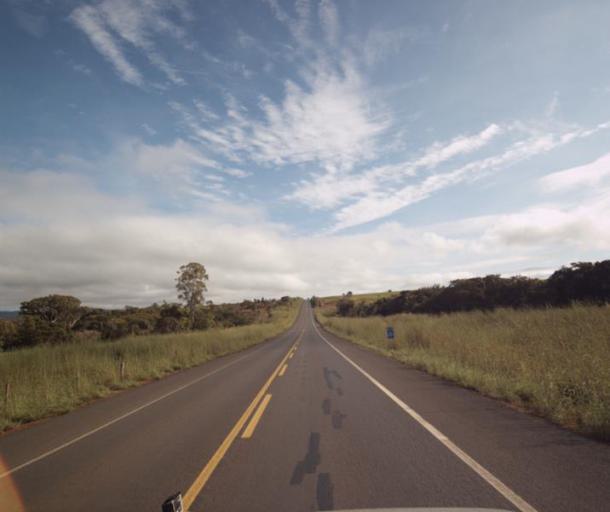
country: BR
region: Goias
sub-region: Padre Bernardo
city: Padre Bernardo
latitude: -15.4364
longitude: -48.6197
